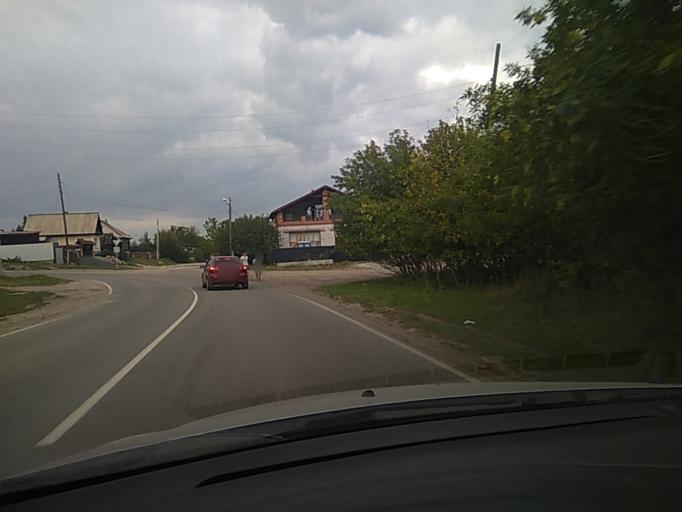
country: RU
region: Chelyabinsk
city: Kyshtym
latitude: 55.7125
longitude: 60.5135
